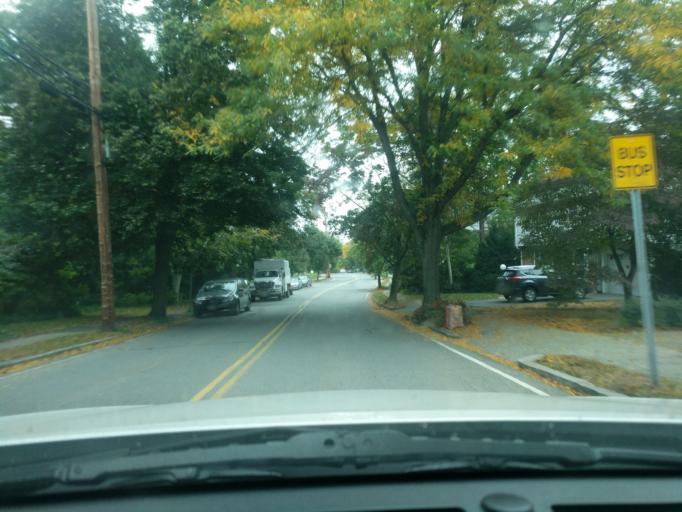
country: US
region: Massachusetts
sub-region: Middlesex County
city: Arlington
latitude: 42.4131
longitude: -71.1609
